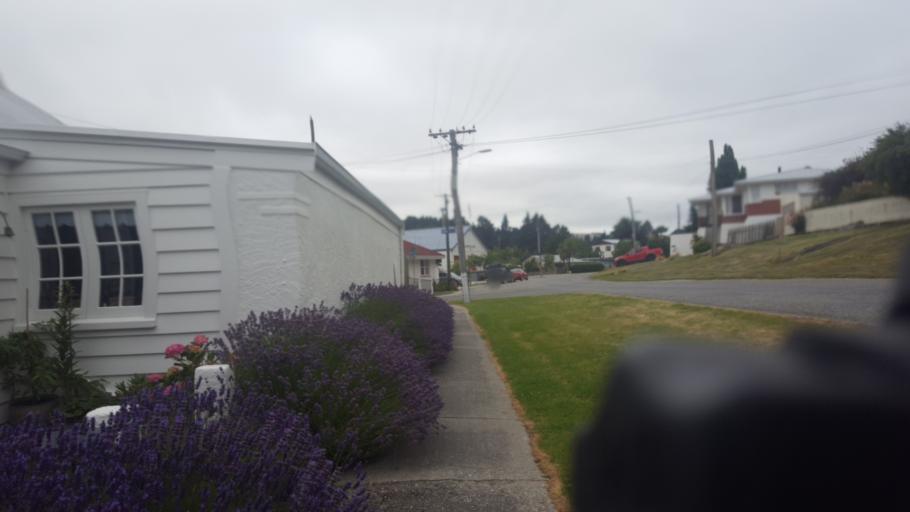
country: NZ
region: Otago
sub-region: Queenstown-Lakes District
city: Kingston
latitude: -45.5407
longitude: 169.3131
